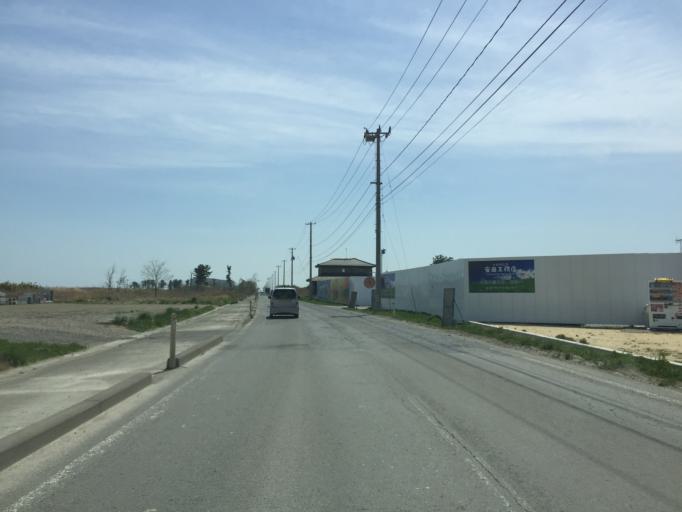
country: JP
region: Miyagi
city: Watari
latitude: 37.9681
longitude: 140.9071
